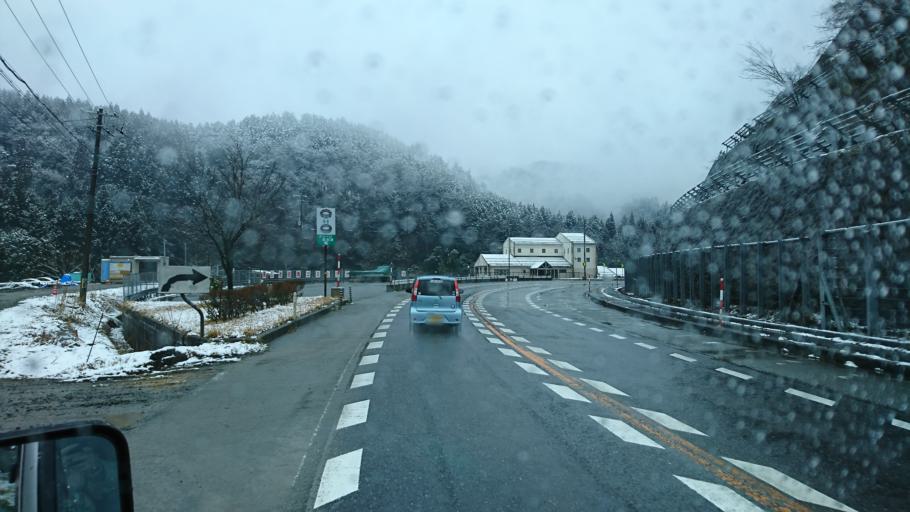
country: JP
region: Hyogo
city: Toyooka
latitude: 35.4774
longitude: 134.5854
